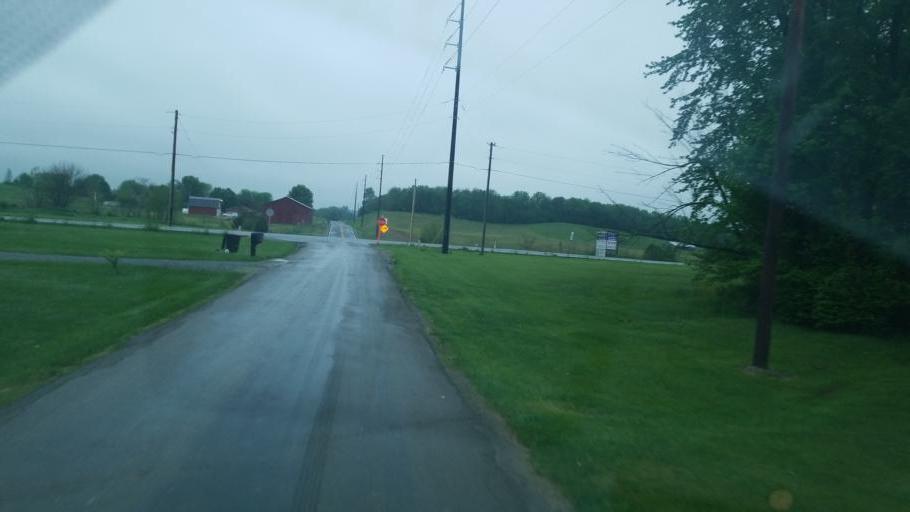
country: US
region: Ohio
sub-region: Highland County
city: Hillsboro
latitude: 39.1873
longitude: -83.6498
